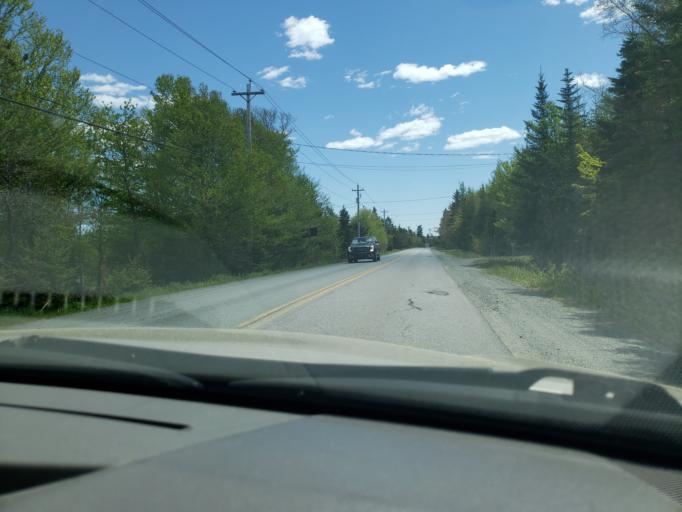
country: CA
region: Nova Scotia
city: Cole Harbour
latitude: 44.7323
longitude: -63.3082
